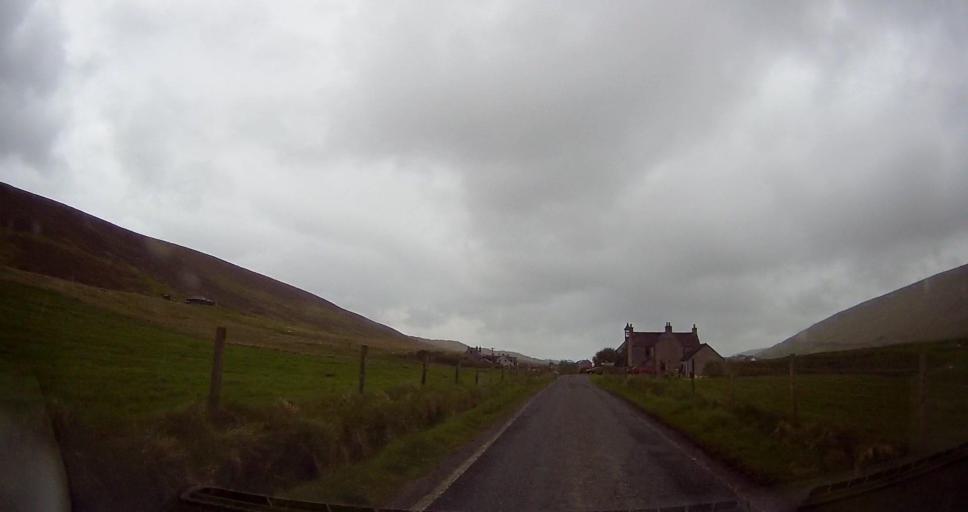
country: GB
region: Scotland
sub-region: Shetland Islands
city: Lerwick
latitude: 60.2571
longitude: -1.2888
